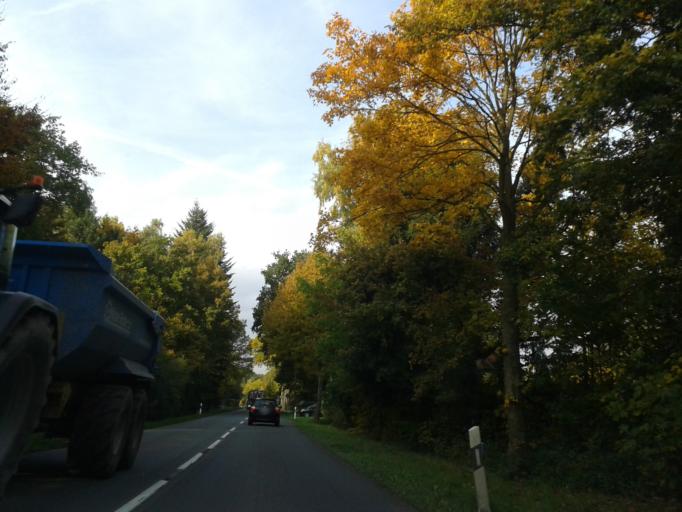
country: DE
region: North Rhine-Westphalia
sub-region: Regierungsbezirk Detmold
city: Hovelhof
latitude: 51.7406
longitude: 8.6607
